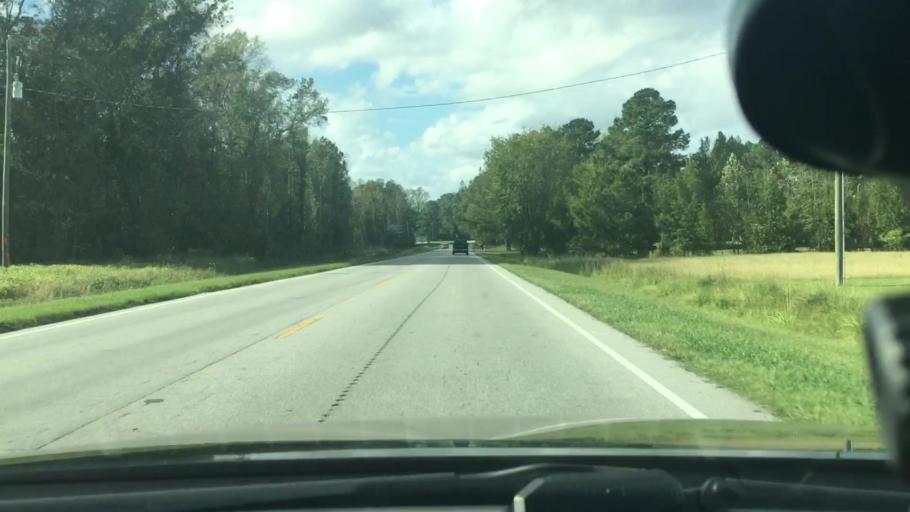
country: US
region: North Carolina
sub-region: Craven County
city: Vanceboro
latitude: 35.2772
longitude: -77.1190
